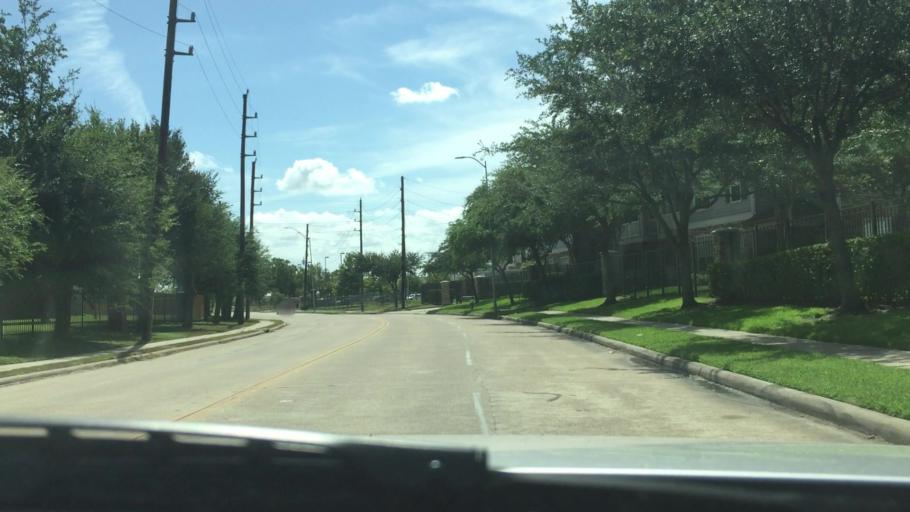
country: US
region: Texas
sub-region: Harris County
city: Bunker Hill Village
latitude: 29.7338
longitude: -95.5979
